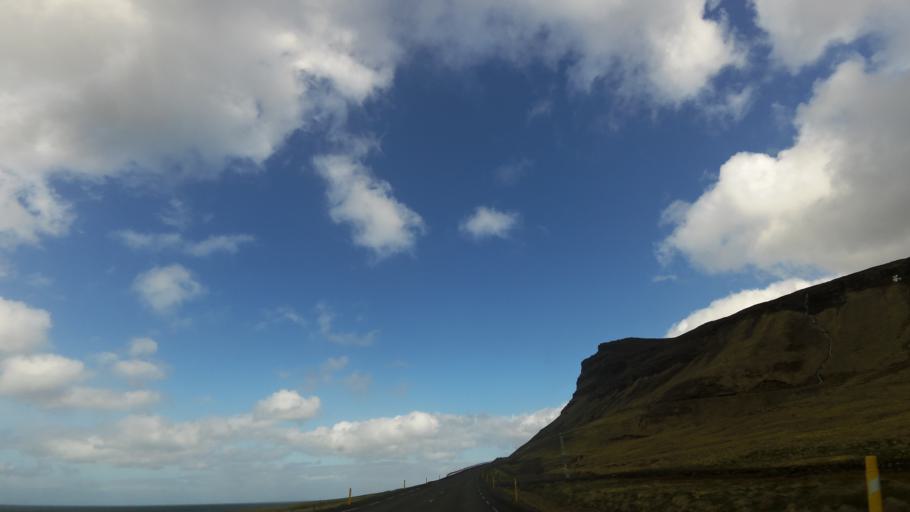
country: IS
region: West
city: Olafsvik
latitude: 64.9358
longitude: -23.5043
